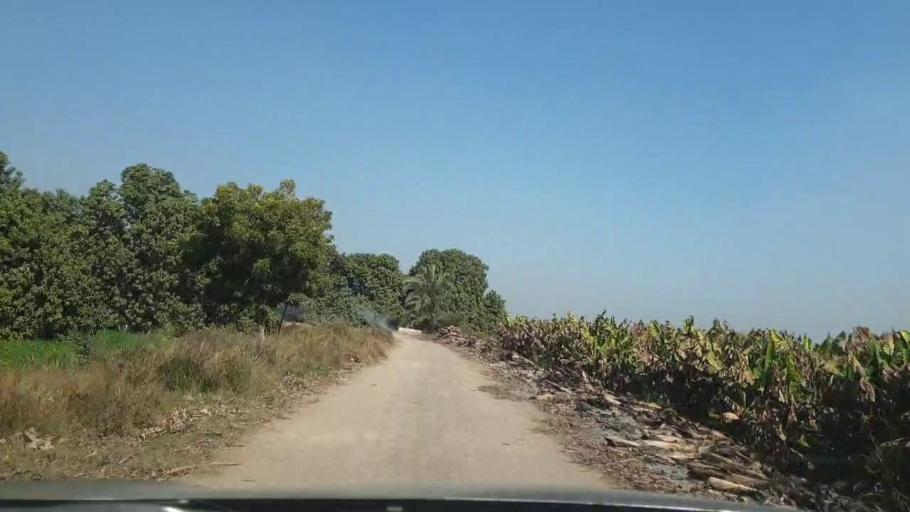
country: PK
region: Sindh
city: Tando Adam
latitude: 25.6214
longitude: 68.6462
